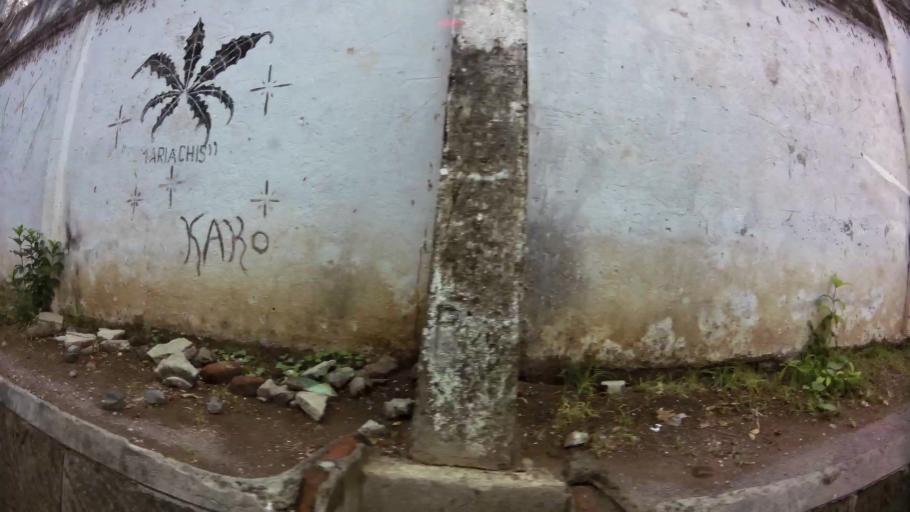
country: NI
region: Granada
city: Granada
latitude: 11.9353
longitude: -85.9467
